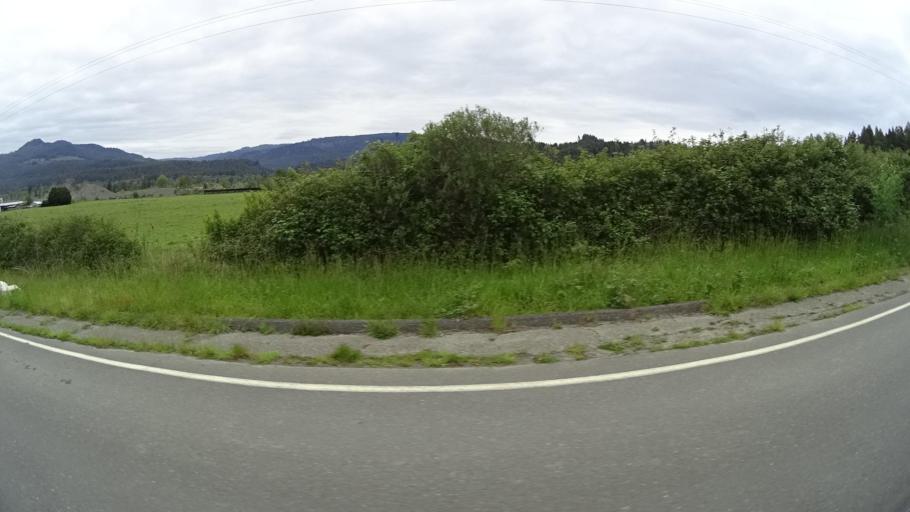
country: US
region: California
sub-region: Humboldt County
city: Blue Lake
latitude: 40.8593
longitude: -123.9960
